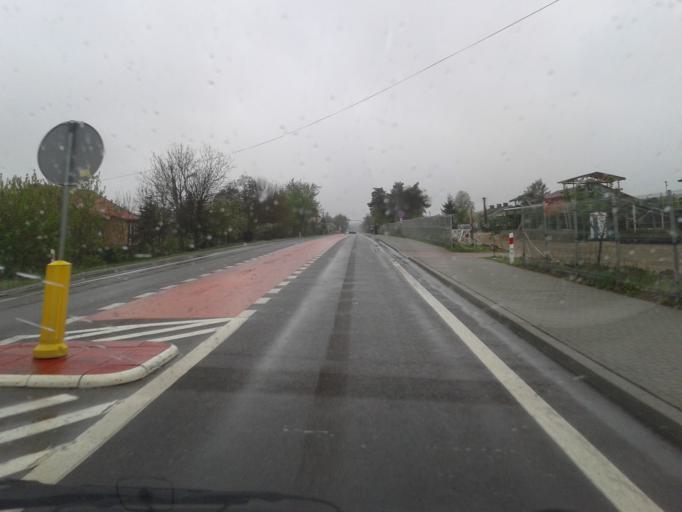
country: PL
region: Lublin Voivodeship
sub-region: Powiat tomaszowski
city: Belzec
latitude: 50.3734
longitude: 23.4537
